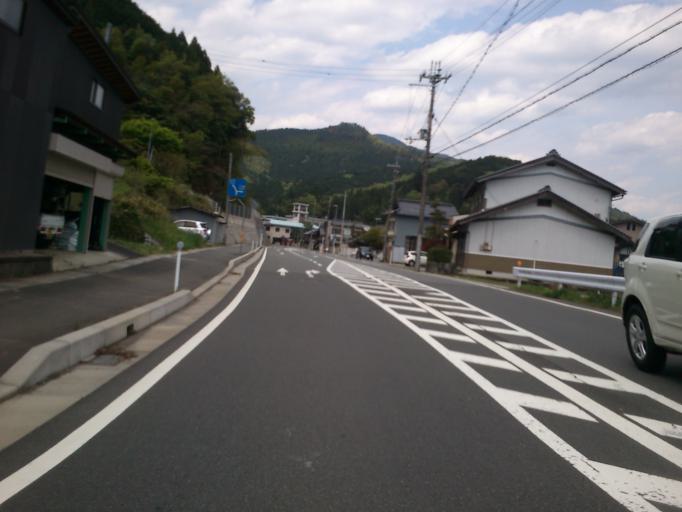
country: JP
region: Kyoto
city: Fukuchiyama
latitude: 35.3483
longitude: 134.9448
